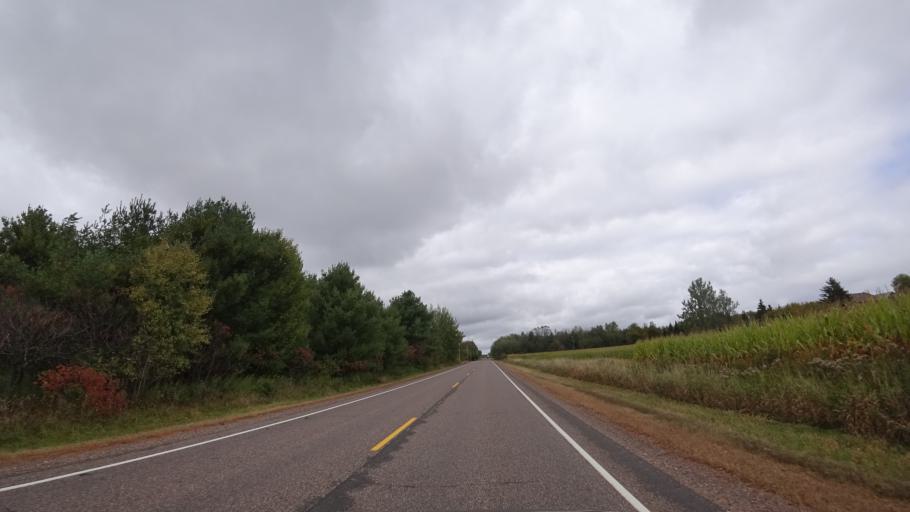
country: US
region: Wisconsin
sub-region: Chippewa County
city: Lake Wissota
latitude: 45.0184
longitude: -91.2868
